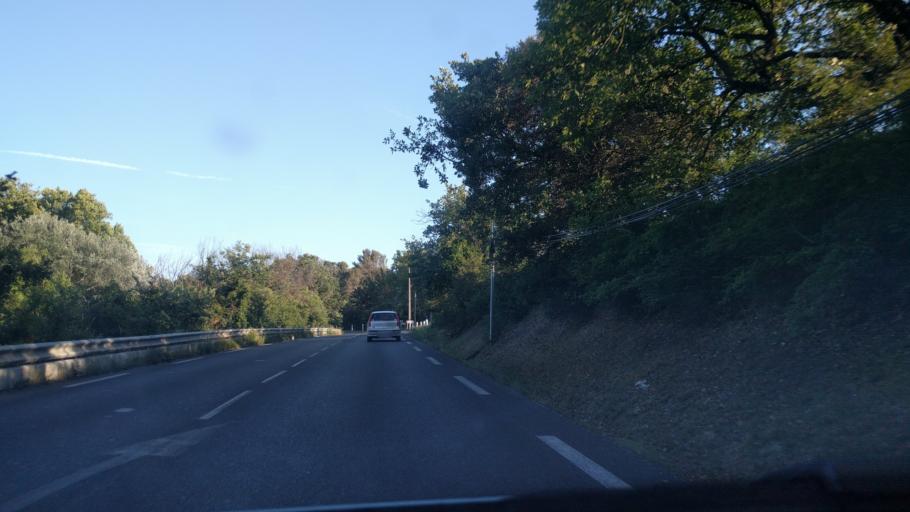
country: FR
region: Provence-Alpes-Cote d'Azur
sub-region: Departement des Bouches-du-Rhone
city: Venelles
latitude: 43.6239
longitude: 5.4902
